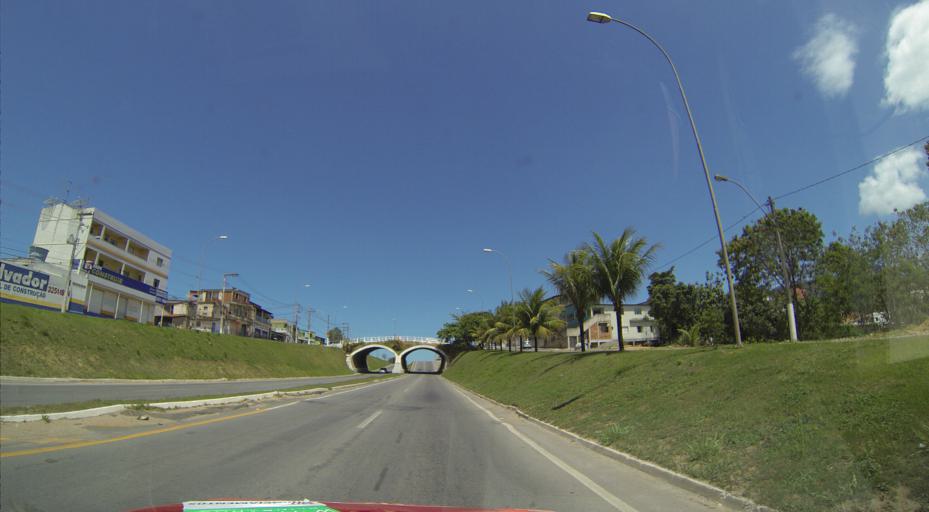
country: BR
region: Espirito Santo
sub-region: Serra
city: Serra
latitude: -20.1226
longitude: -40.3057
